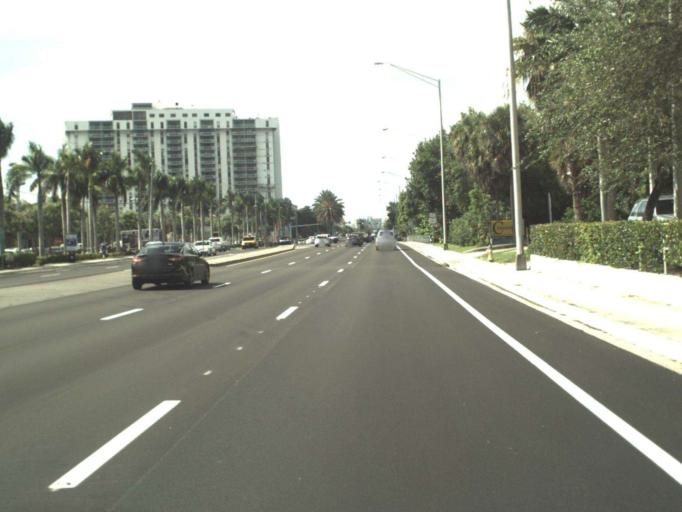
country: US
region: Florida
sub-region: Miami-Dade County
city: Biscayne Park
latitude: 25.9030
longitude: -80.1597
